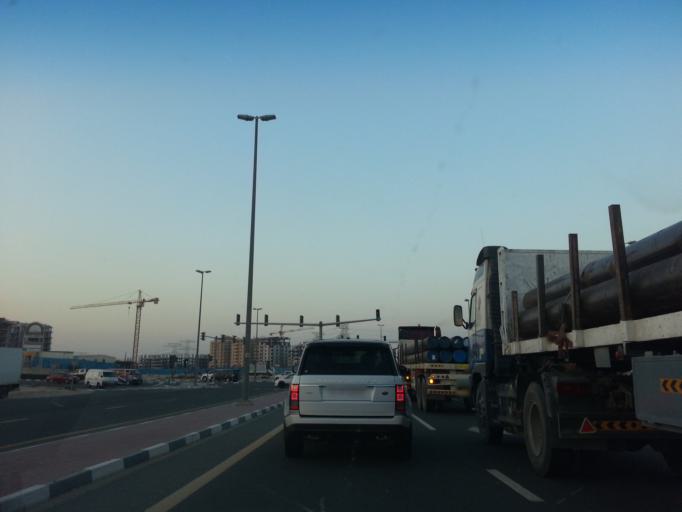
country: AE
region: Dubai
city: Dubai
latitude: 24.9872
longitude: 55.1856
